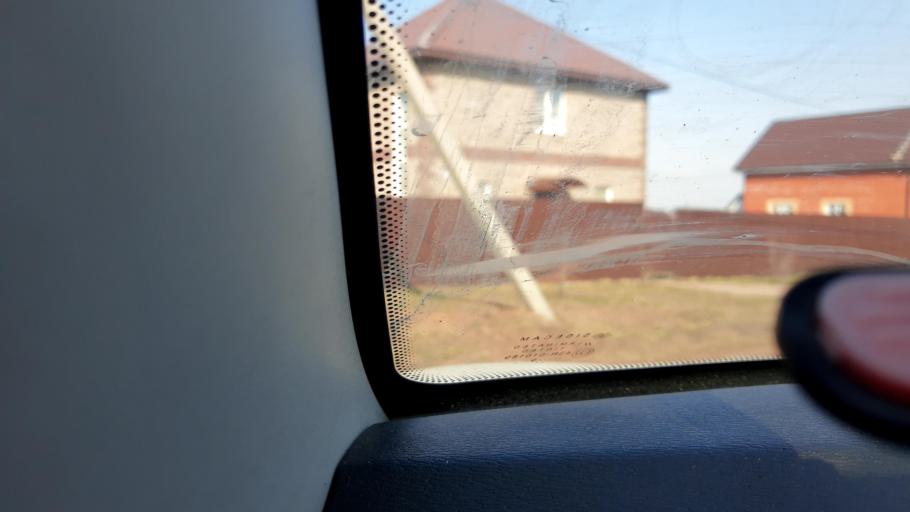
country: RU
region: Bashkortostan
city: Kabakovo
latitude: 54.6156
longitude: 56.0918
